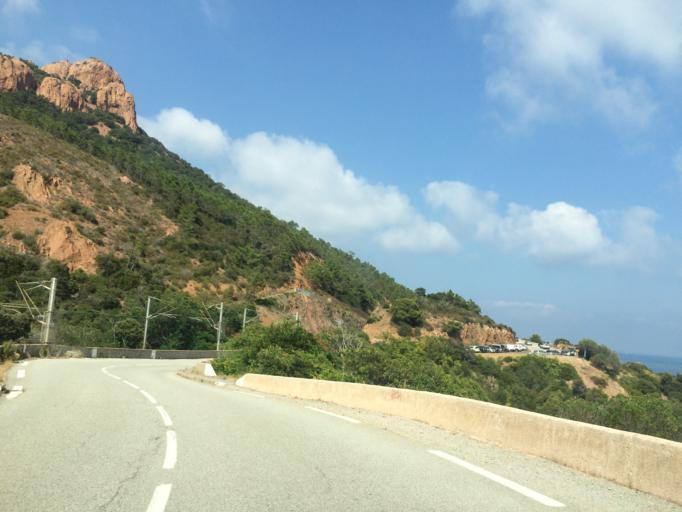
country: FR
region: Provence-Alpes-Cote d'Azur
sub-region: Departement des Alpes-Maritimes
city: Theoule-sur-Mer
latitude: 43.4459
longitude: 6.9057
